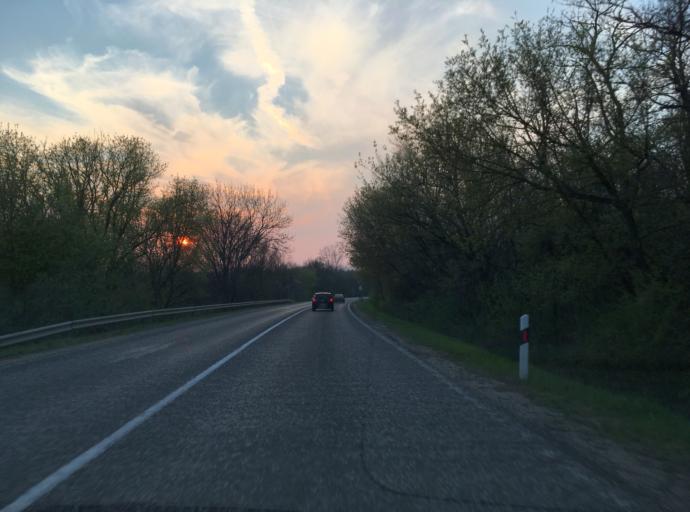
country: HU
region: Fejer
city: Etyek
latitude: 47.4858
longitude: 18.7736
